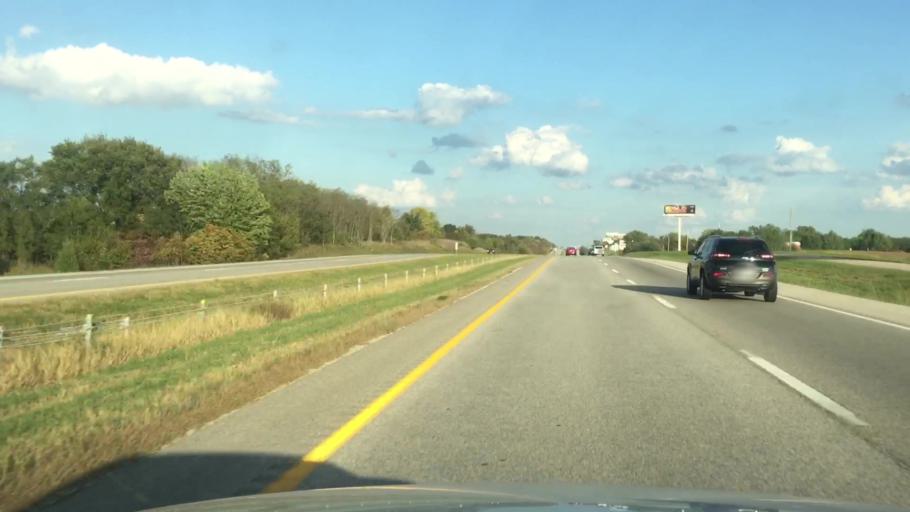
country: US
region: Missouri
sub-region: Saline County
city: Sweet Springs
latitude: 38.9736
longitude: -93.3167
